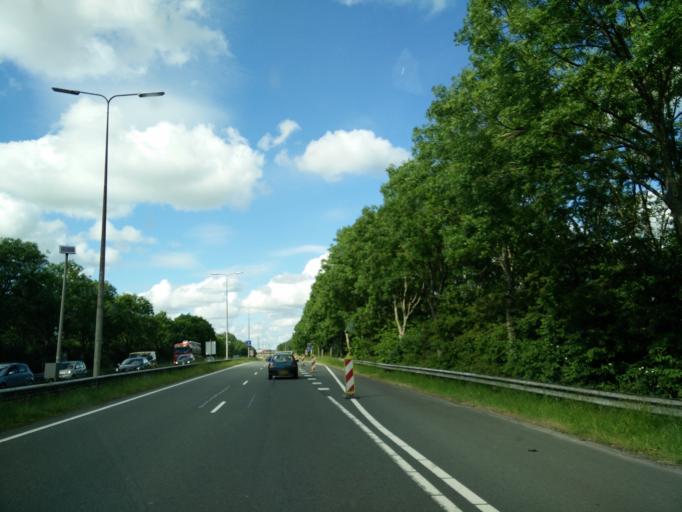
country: NL
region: Groningen
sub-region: Gemeente Groningen
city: Korrewegwijk
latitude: 53.2440
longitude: 6.5707
